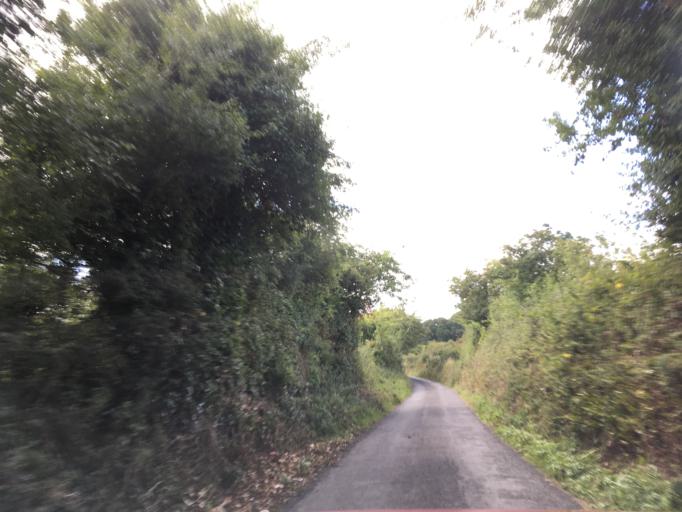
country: IE
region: Munster
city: Cashel
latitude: 52.5204
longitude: -7.8768
